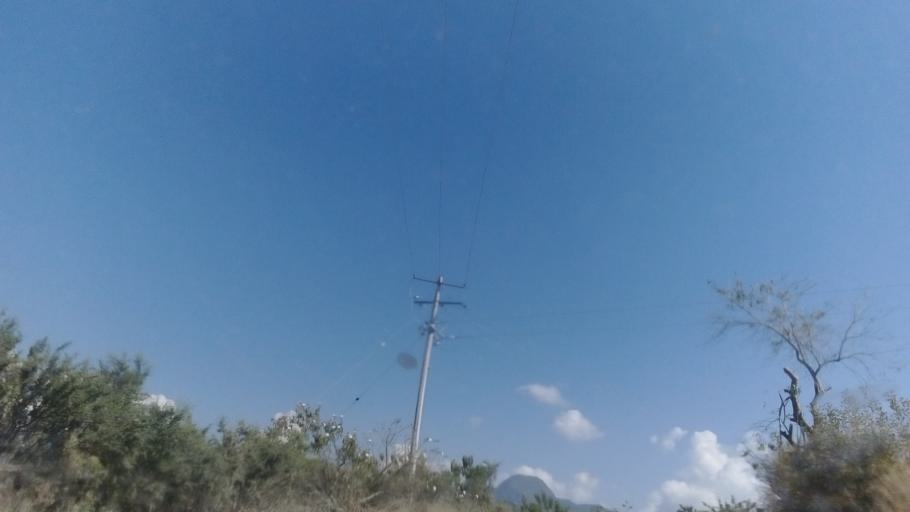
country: MX
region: Guanajuato
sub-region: Leon
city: Medina
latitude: 21.1506
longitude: -101.6022
